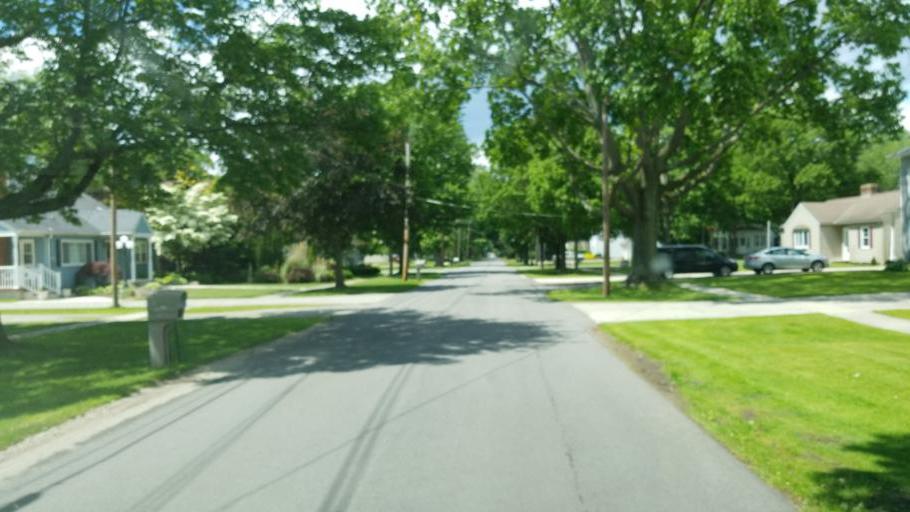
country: US
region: Ohio
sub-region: Erie County
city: Milan
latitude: 41.2943
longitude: -82.5997
